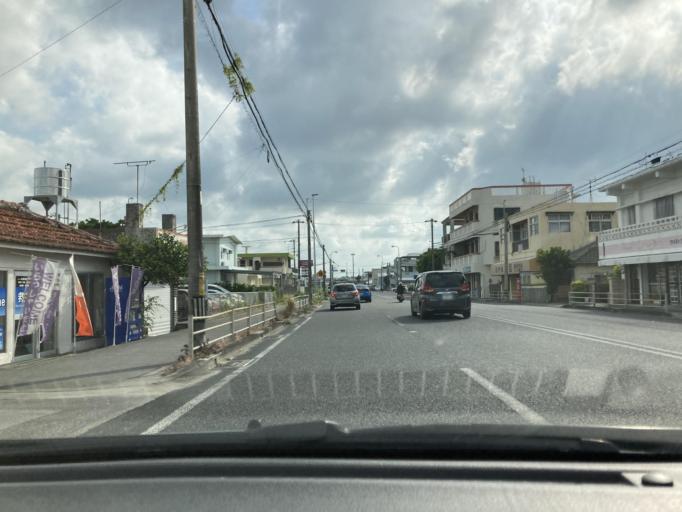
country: JP
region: Okinawa
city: Ginowan
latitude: 26.2189
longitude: 127.7647
